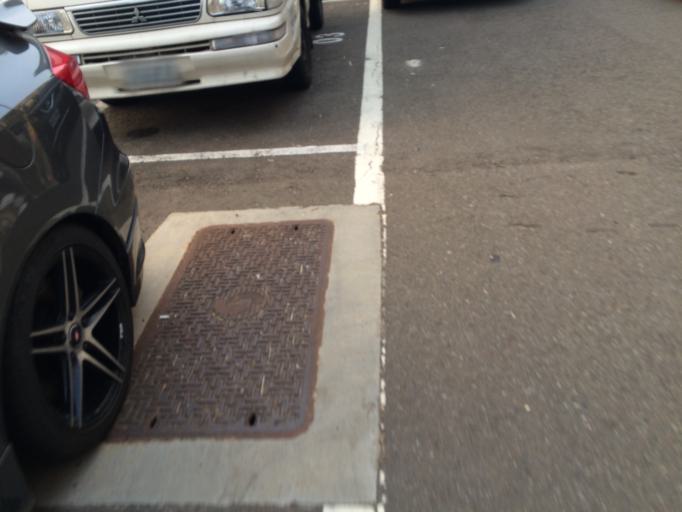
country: TW
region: Taiwan
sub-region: Hsinchu
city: Hsinchu
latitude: 24.7981
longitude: 120.9596
